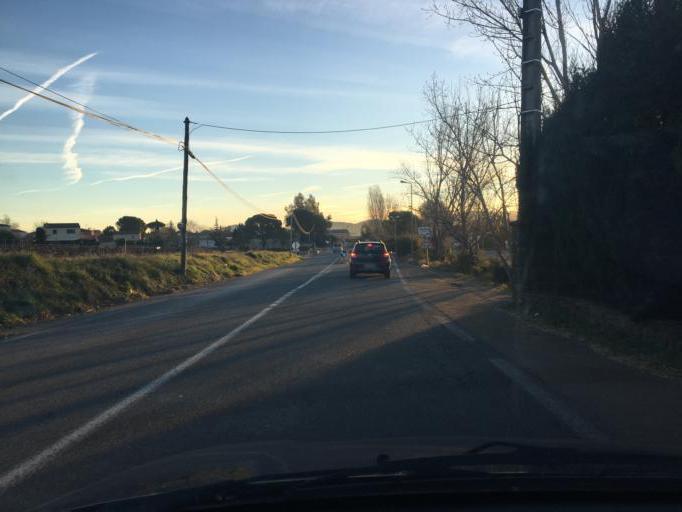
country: FR
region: Provence-Alpes-Cote d'Azur
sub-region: Departement du Var
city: Les Arcs
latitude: 43.4492
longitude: 6.4722
